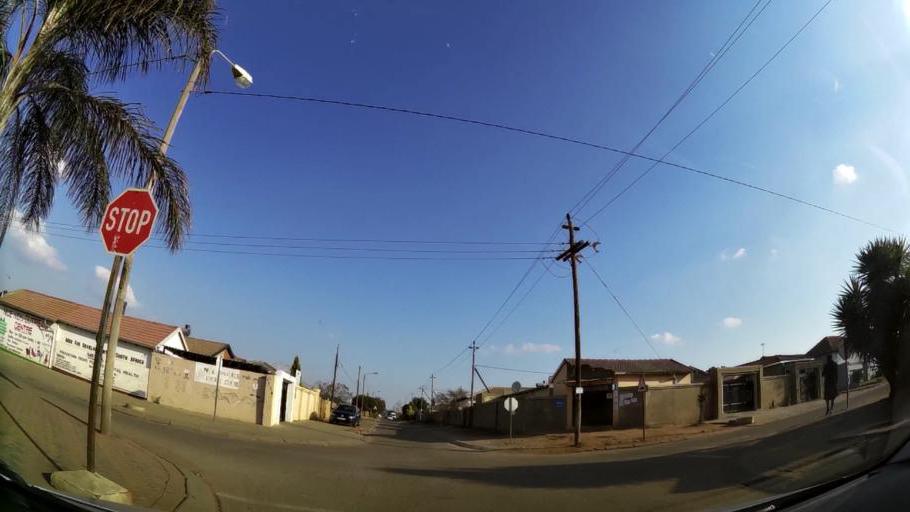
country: ZA
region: Gauteng
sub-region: Ekurhuleni Metropolitan Municipality
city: Tembisa
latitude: -25.9535
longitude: 28.2027
